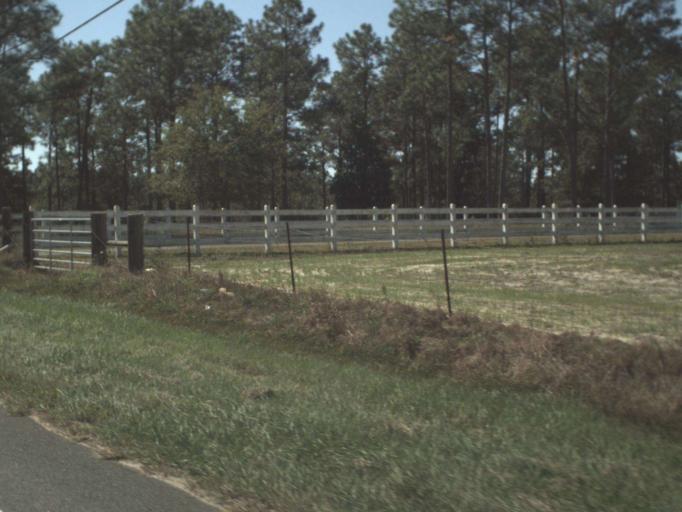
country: US
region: Florida
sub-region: Walton County
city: DeFuniak Springs
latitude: 30.7946
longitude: -86.1220
